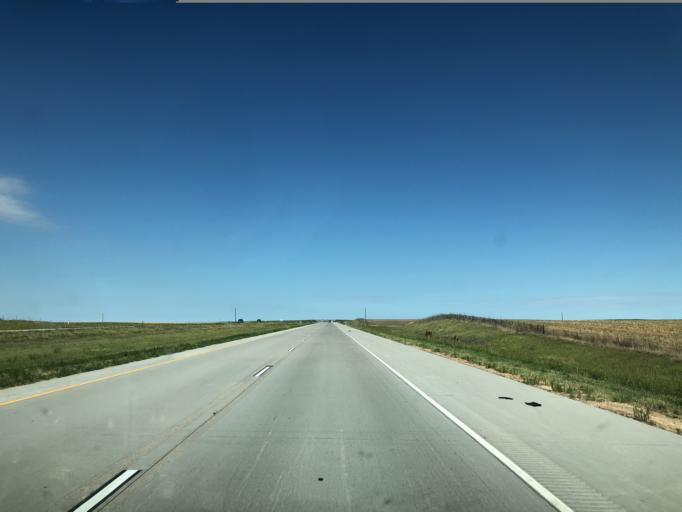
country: US
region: Colorado
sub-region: Kit Carson County
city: Burlington
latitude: 39.2941
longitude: -102.7568
